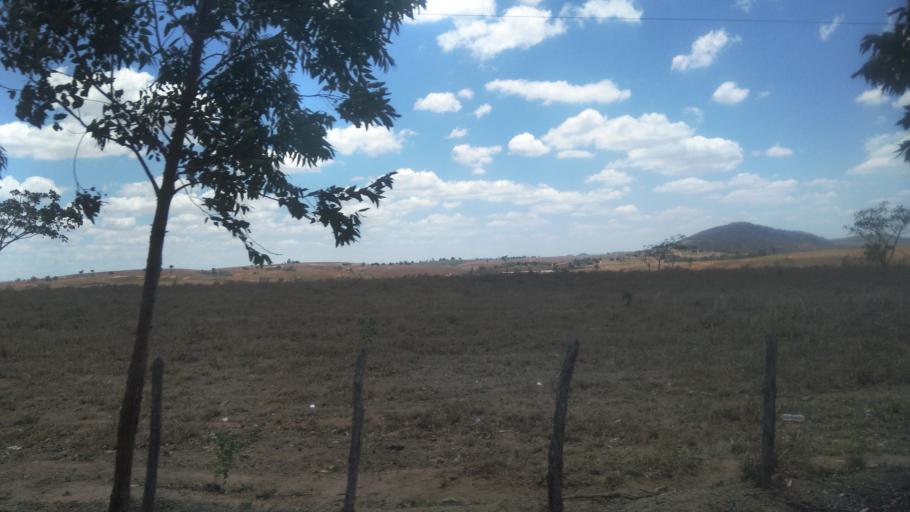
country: BR
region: Pernambuco
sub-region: Nazare Da Mata
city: Nazare da Mata
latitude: -7.7341
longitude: -35.2779
